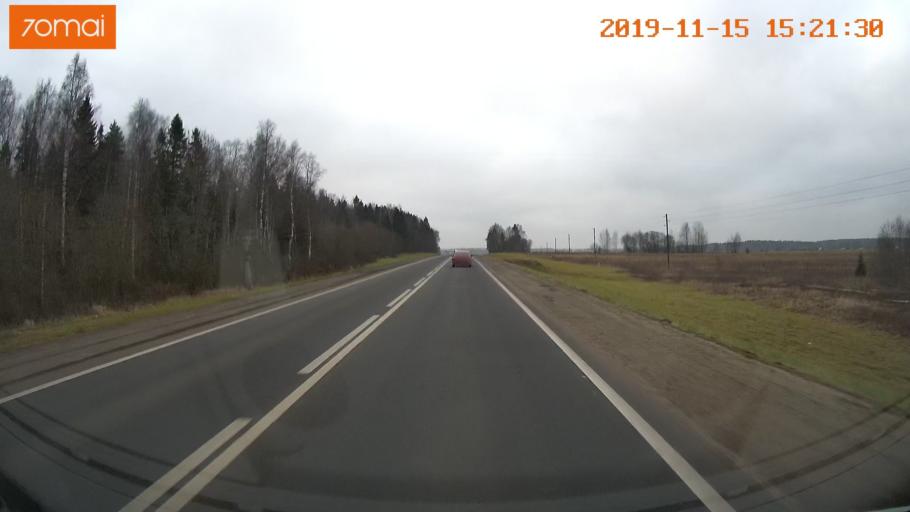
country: RU
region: Jaroslavl
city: Danilov
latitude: 58.2118
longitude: 40.1445
